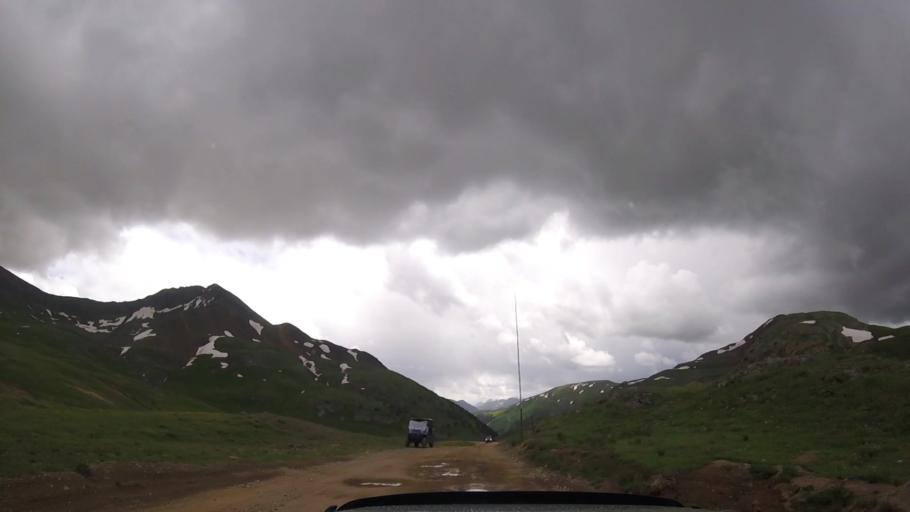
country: US
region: Colorado
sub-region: Ouray County
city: Ouray
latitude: 37.9548
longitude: -107.5749
